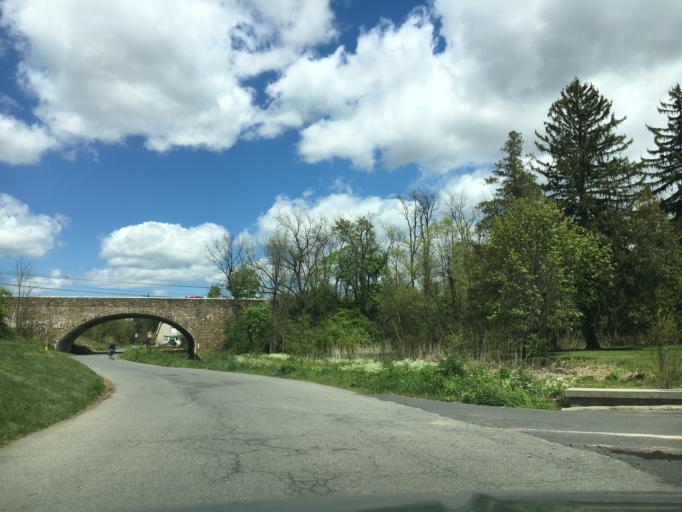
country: US
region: Pennsylvania
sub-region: Lehigh County
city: Dorneyville
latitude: 40.5946
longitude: -75.5356
